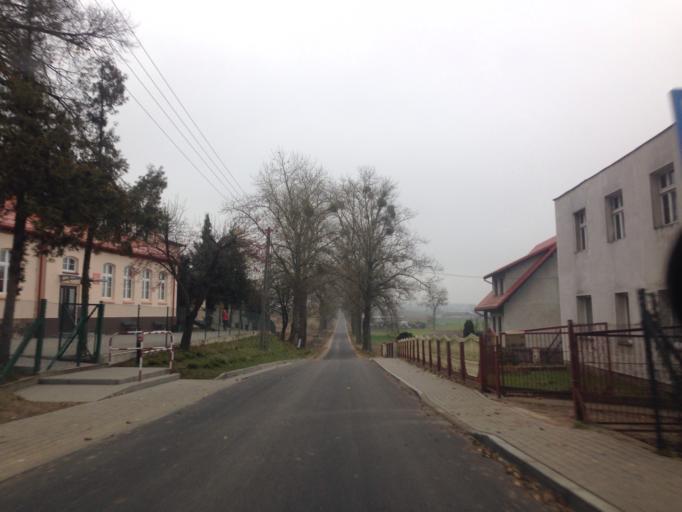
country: PL
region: Kujawsko-Pomorskie
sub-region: Powiat brodnicki
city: Bartniczka
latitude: 53.2568
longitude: 19.6395
